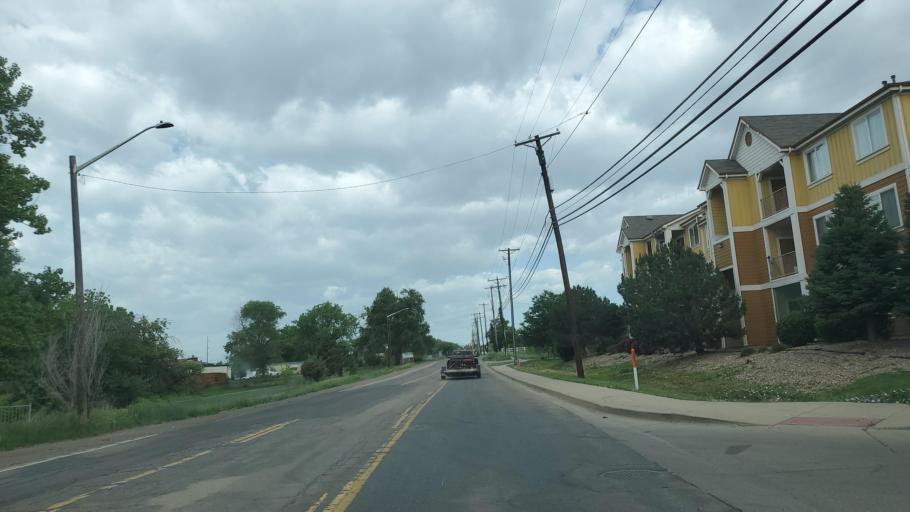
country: US
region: Colorado
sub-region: Adams County
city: Welby
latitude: 39.8382
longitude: -104.9664
